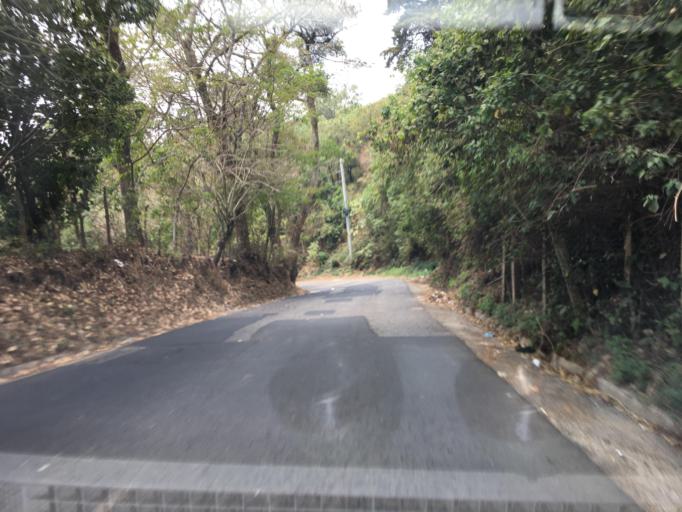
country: GT
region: Escuintla
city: San Vicente Pacaya
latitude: 14.3899
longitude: -90.5507
